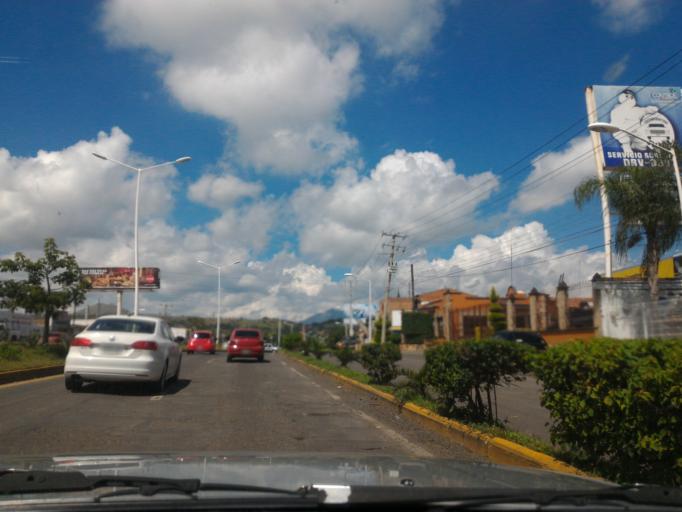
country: MX
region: Jalisco
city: Tequila
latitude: 20.8806
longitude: -103.8294
